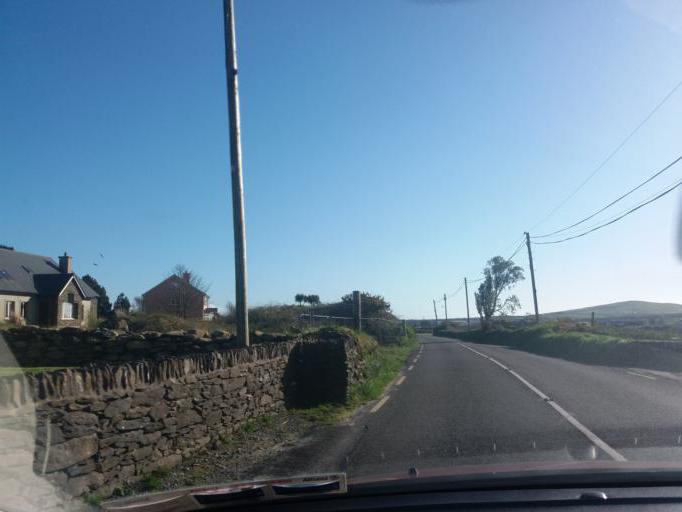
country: IE
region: Munster
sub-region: Ciarrai
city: Dingle
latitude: 52.1542
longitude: -10.2886
